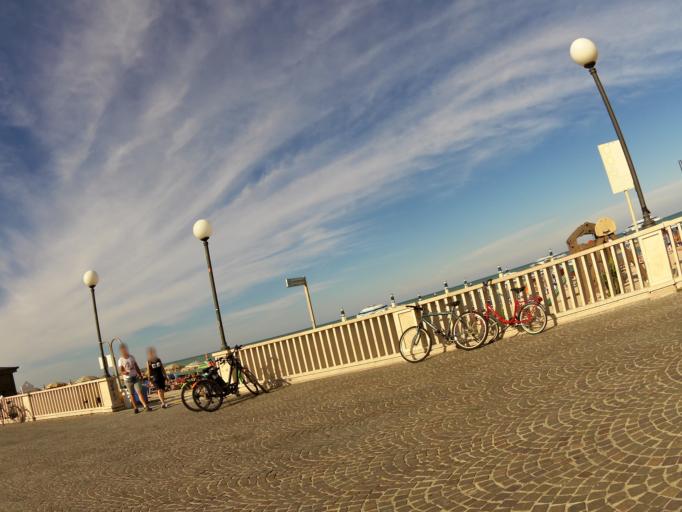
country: IT
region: The Marches
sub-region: Provincia di Macerata
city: Porto Recanati
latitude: 43.4360
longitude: 13.6641
